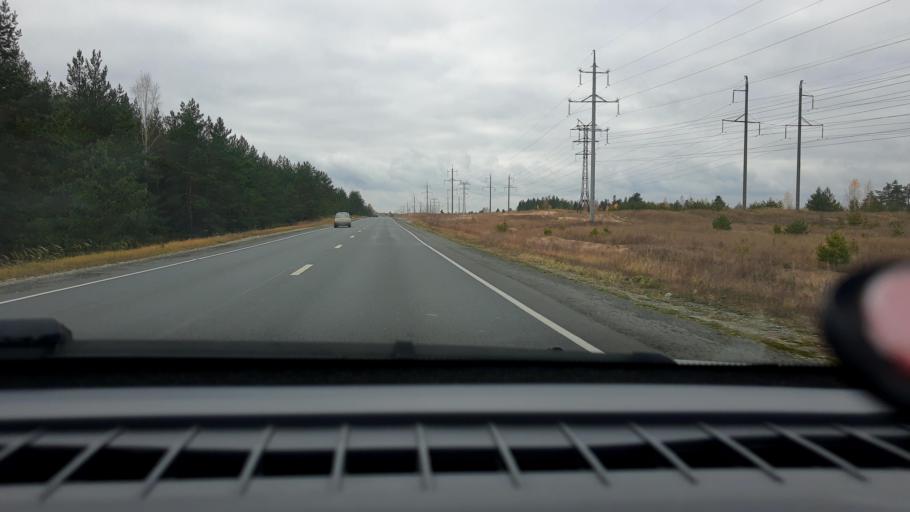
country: RU
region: Nizjnij Novgorod
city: Lukino
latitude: 56.3829
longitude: 43.6333
